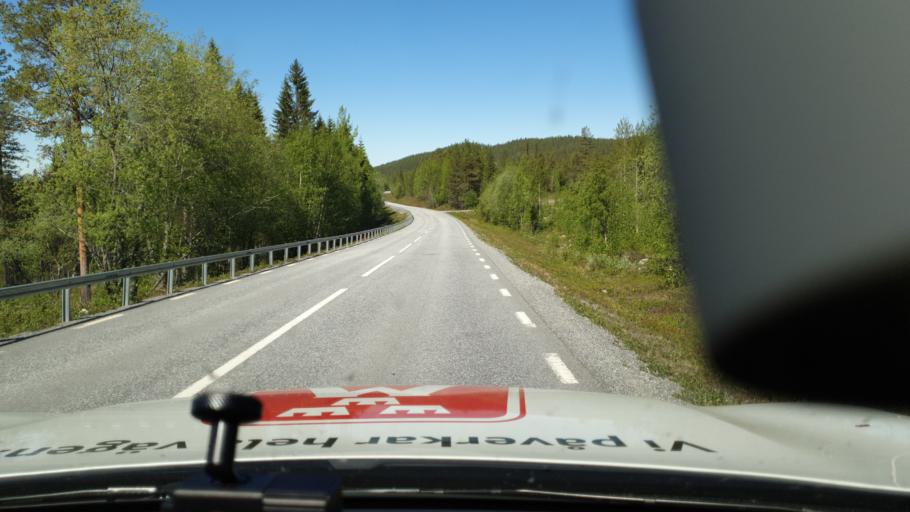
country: SE
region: Vaesterbotten
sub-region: Storumans Kommun
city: Storuman
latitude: 65.1493
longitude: 17.0730
